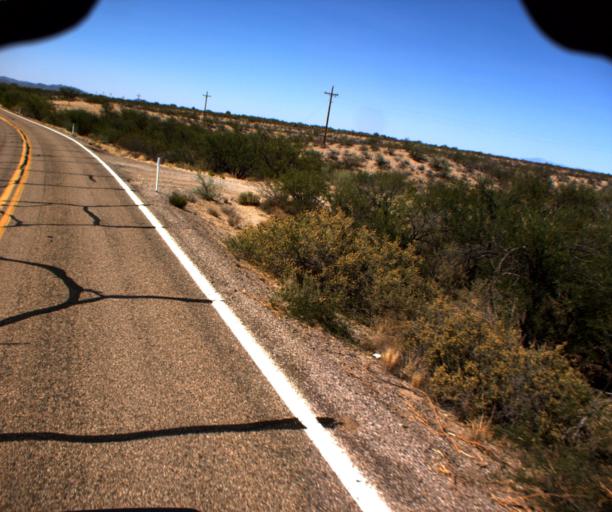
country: US
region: Arizona
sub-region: Pima County
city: Three Points
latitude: 31.9383
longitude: -111.3906
